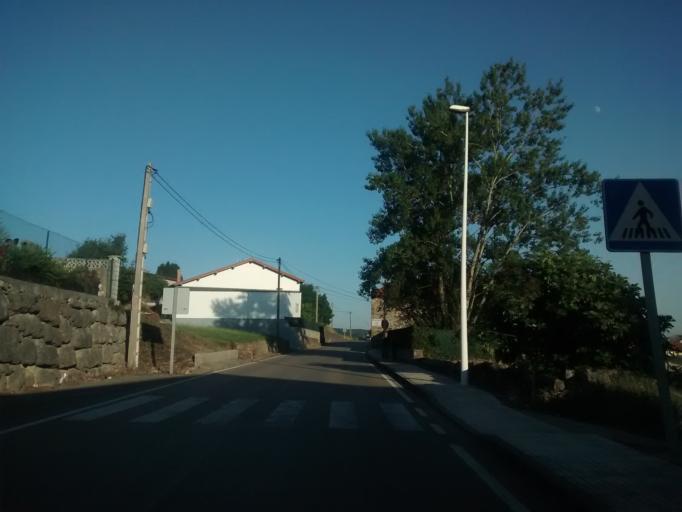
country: ES
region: Cantabria
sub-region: Provincia de Cantabria
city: San Miguel de Meruelo
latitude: 43.4595
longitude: -3.5829
